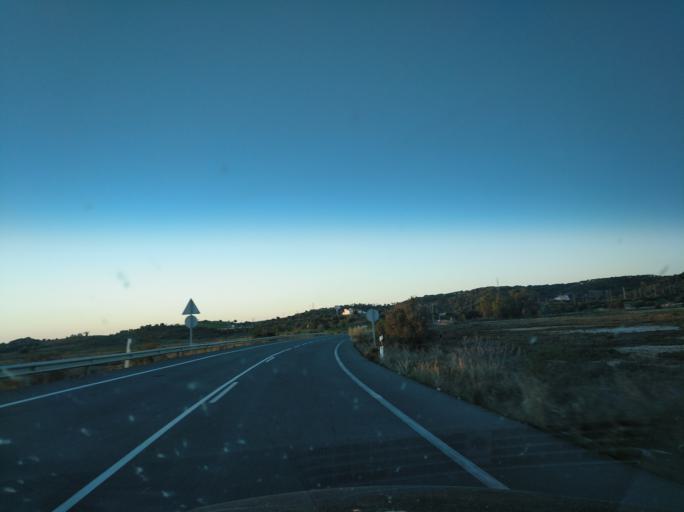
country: ES
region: Andalusia
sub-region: Provincia de Huelva
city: Ayamonte
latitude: 37.2327
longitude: -7.4035
